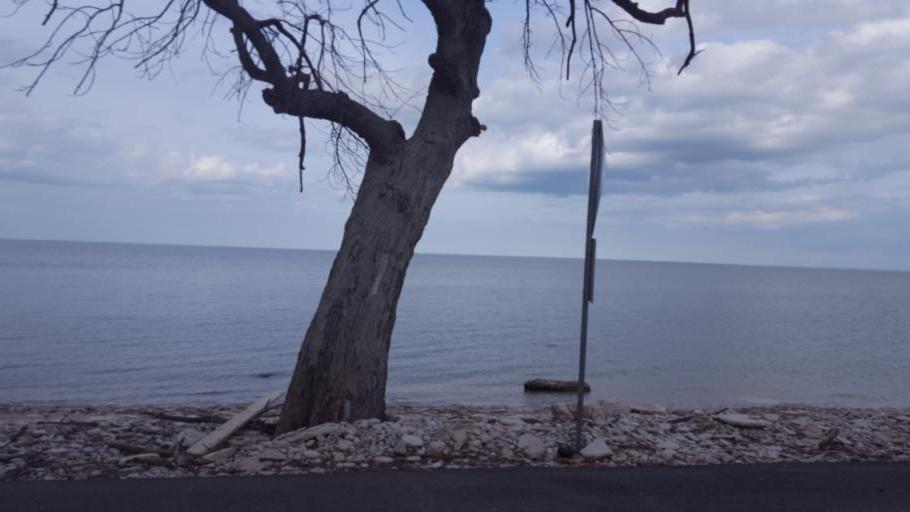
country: US
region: Ohio
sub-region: Erie County
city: Sandusky
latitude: 41.5293
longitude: -82.7133
